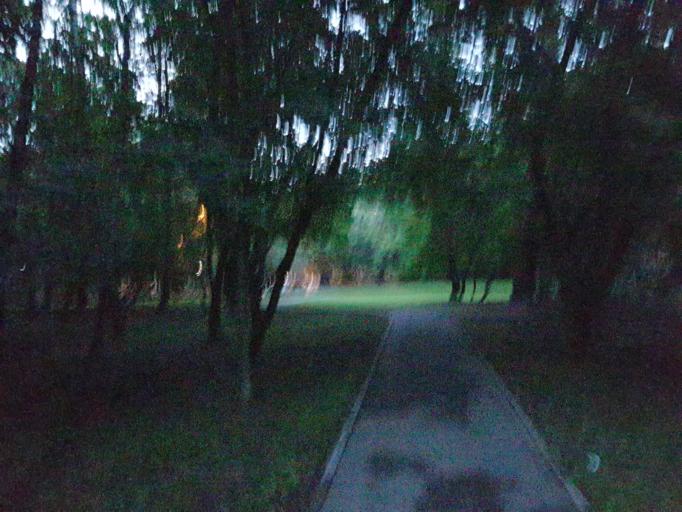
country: RU
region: Moscow
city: Nagornyy
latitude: 55.6538
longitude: 37.6112
